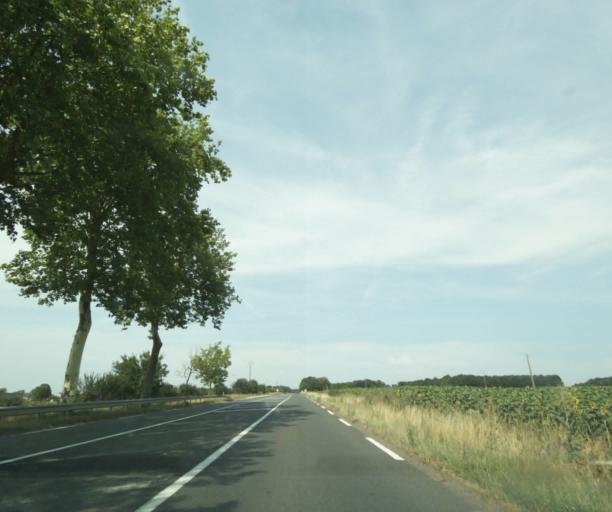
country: FR
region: Centre
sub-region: Departement d'Indre-et-Loire
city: Sainte-Maure-de-Touraine
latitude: 47.1324
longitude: 0.6340
